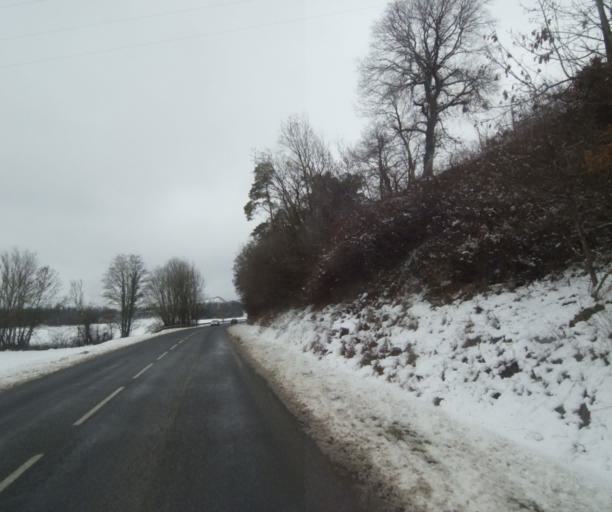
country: FR
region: Champagne-Ardenne
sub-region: Departement de la Haute-Marne
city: Wassy
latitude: 48.4804
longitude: 4.9703
